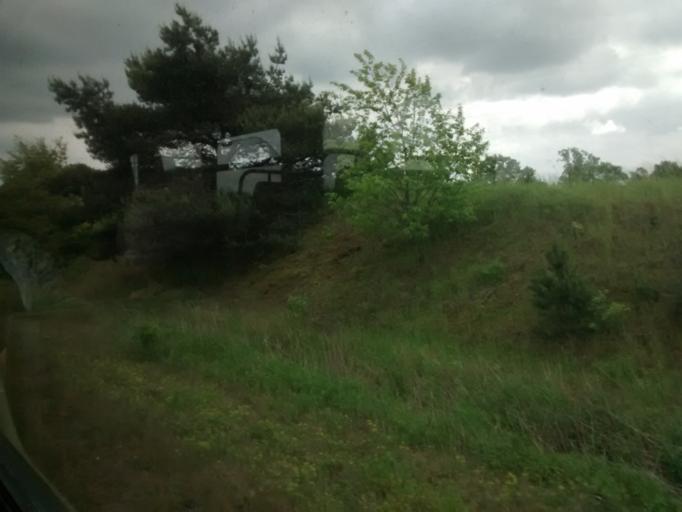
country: DE
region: Brandenburg
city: Glienicke
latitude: 52.6611
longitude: 13.3573
